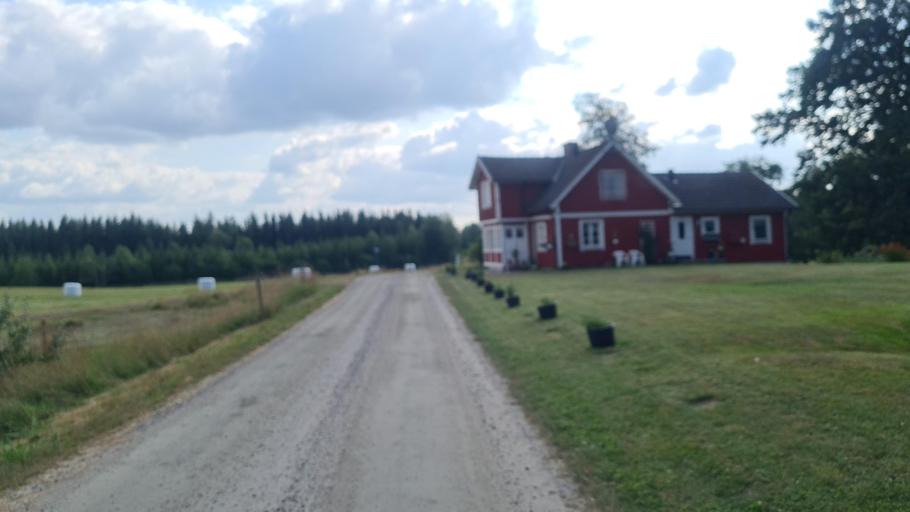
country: SE
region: Kronoberg
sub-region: Ljungby Kommun
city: Ljungby
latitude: 56.7180
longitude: 13.8779
